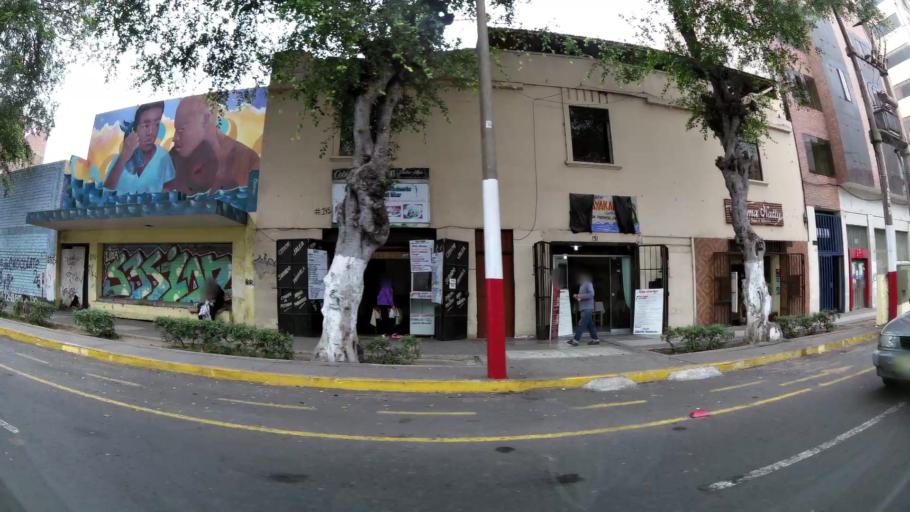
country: PE
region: Callao
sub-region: Callao
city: Callao
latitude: -12.0613
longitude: -77.1466
